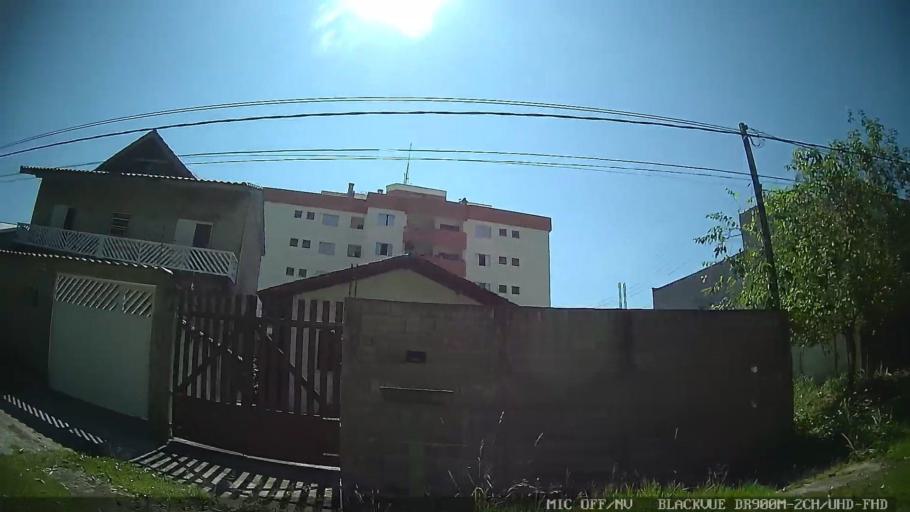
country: BR
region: Sao Paulo
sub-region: Peruibe
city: Peruibe
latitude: -24.2929
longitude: -46.9742
